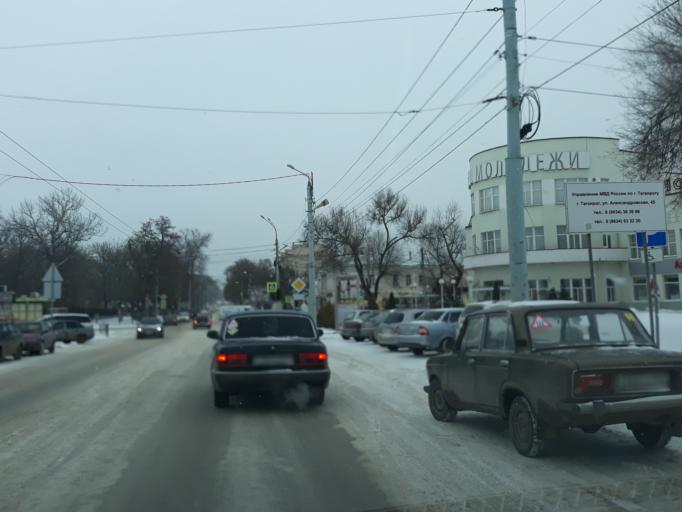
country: RU
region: Rostov
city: Taganrog
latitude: 47.2209
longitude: 38.9205
